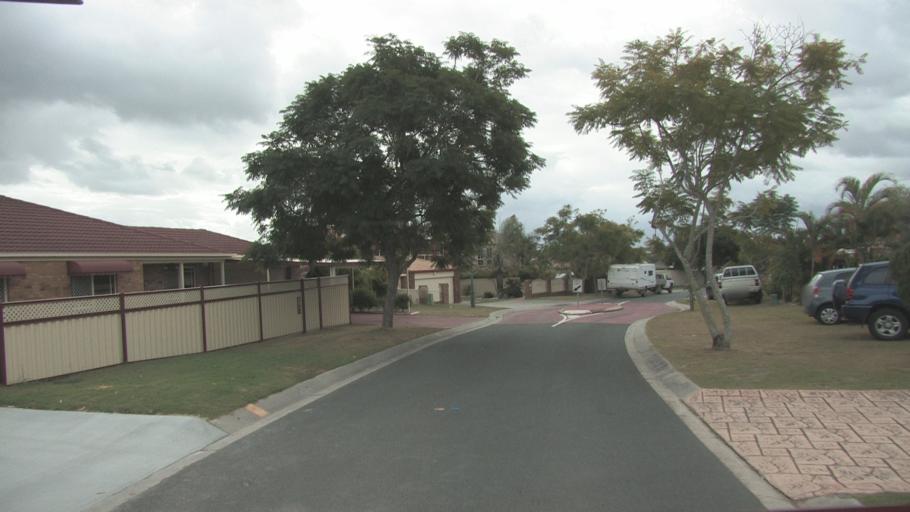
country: AU
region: Queensland
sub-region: Logan
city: Park Ridge South
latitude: -27.6889
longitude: 153.0534
